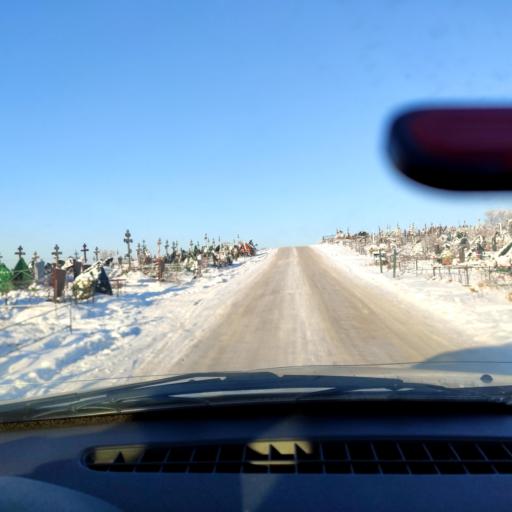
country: RU
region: Bashkortostan
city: Ufa
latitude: 54.8565
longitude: 56.1659
